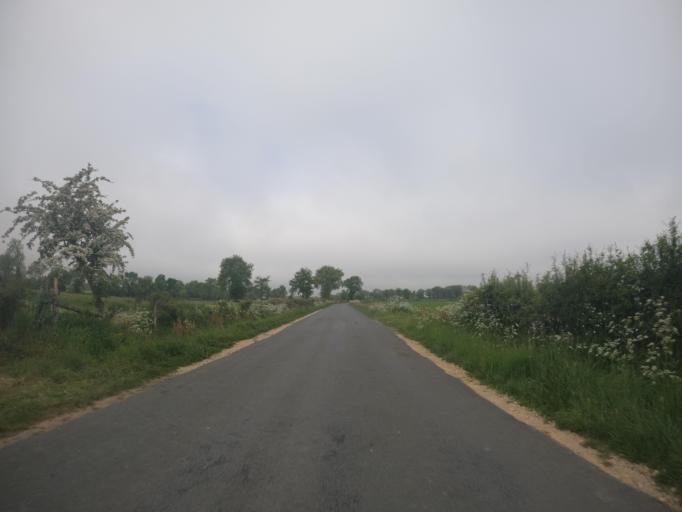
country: FR
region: Poitou-Charentes
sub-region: Departement des Deux-Sevres
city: Saint-Varent
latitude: 46.8749
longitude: -0.3169
